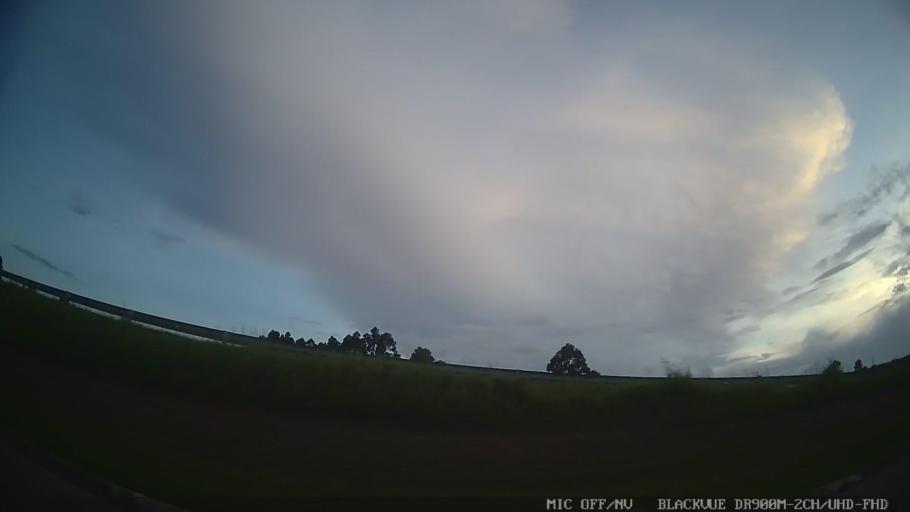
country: BR
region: Sao Paulo
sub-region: Cabreuva
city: Cabreuva
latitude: -23.2623
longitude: -47.1878
